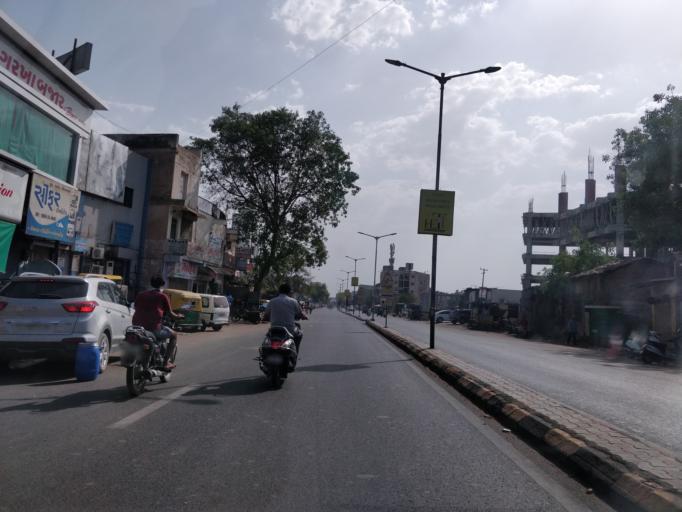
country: IN
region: Gujarat
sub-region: Ahmadabad
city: Naroda
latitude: 23.0745
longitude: 72.6552
